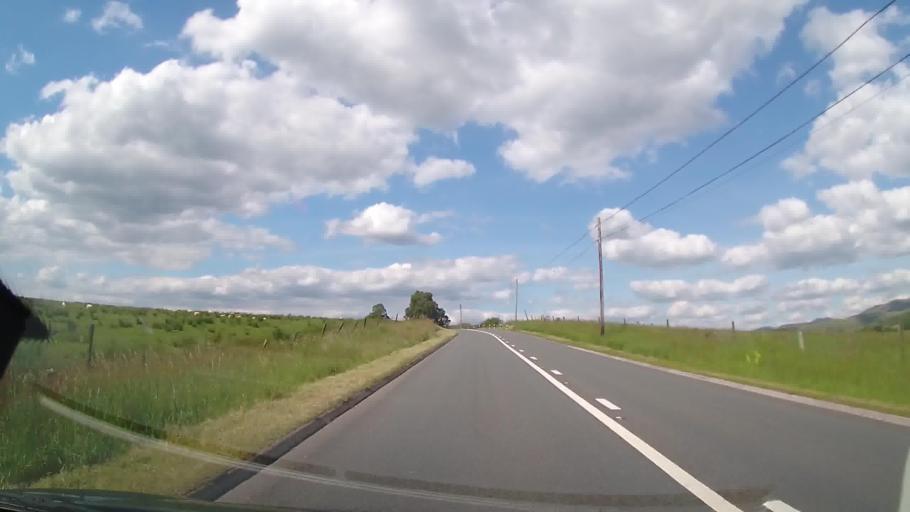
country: GB
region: Wales
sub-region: Gwynedd
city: Dolgellau
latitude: 52.7288
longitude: -3.8284
